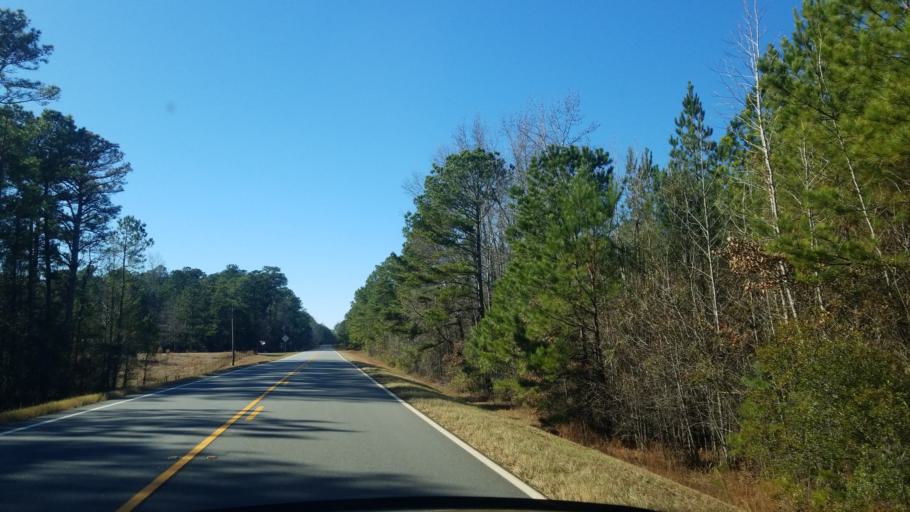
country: US
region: Georgia
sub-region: Talbot County
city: Sardis
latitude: 32.6328
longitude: -84.7281
